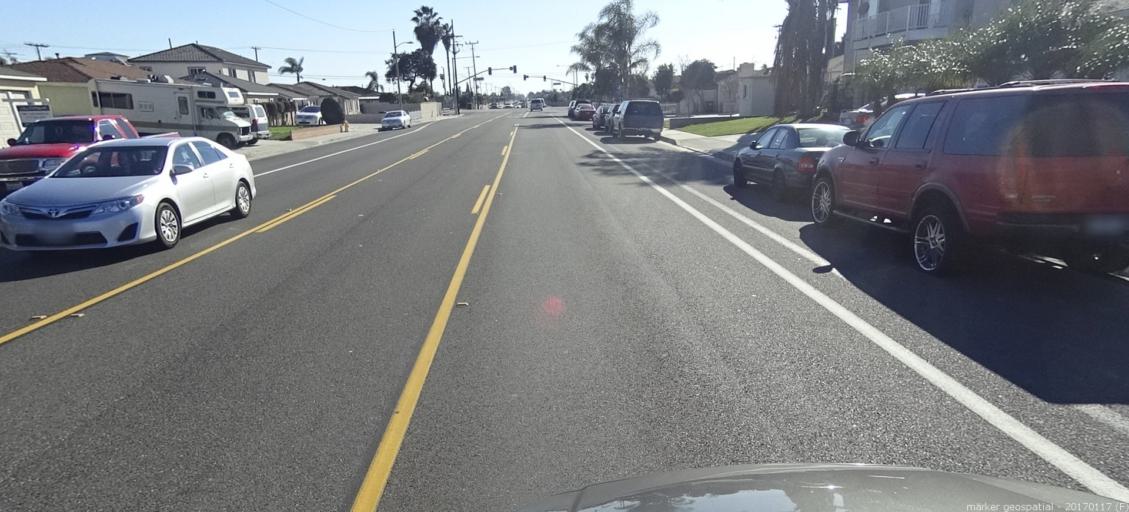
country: US
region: California
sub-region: Orange County
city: Midway City
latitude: 33.7461
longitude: -117.9810
